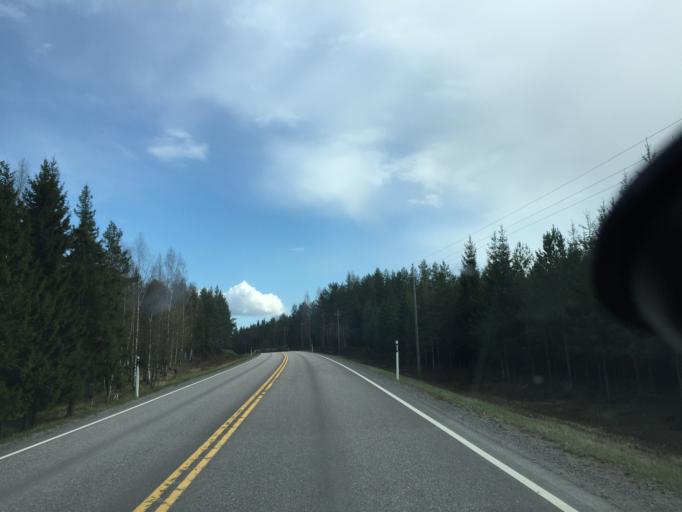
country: FI
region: Uusimaa
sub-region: Raaseporin
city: Ekenaes
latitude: 60.0428
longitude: 23.3380
